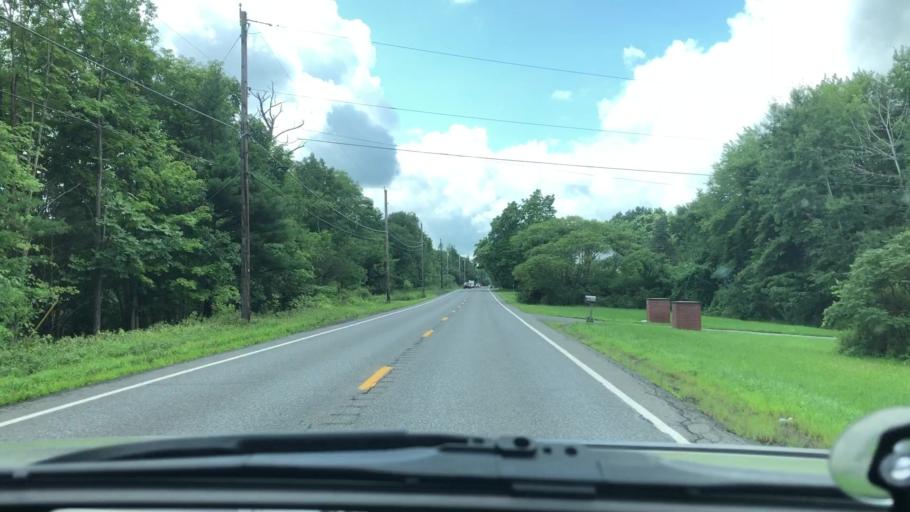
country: US
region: New York
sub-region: Greene County
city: Palenville
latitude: 42.1526
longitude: -73.9996
